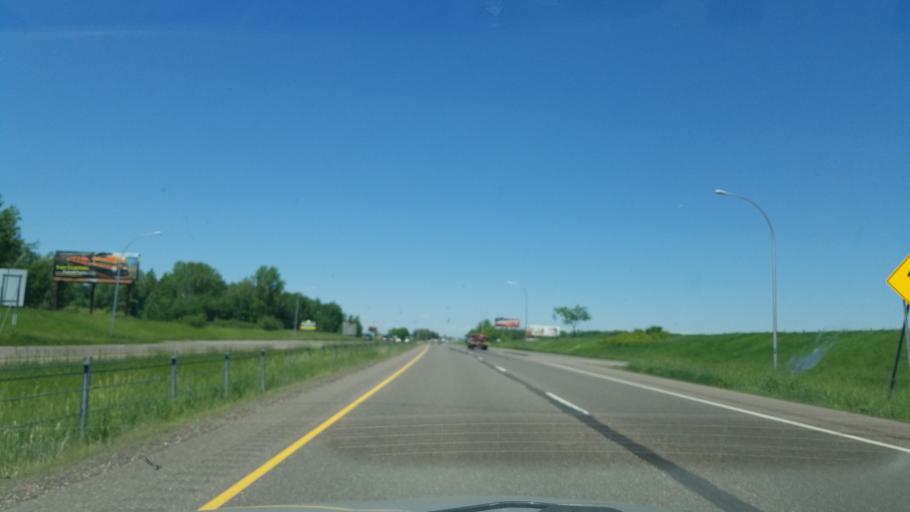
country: US
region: Minnesota
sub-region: Pine County
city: Rock Creek
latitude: 45.7686
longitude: -92.9896
